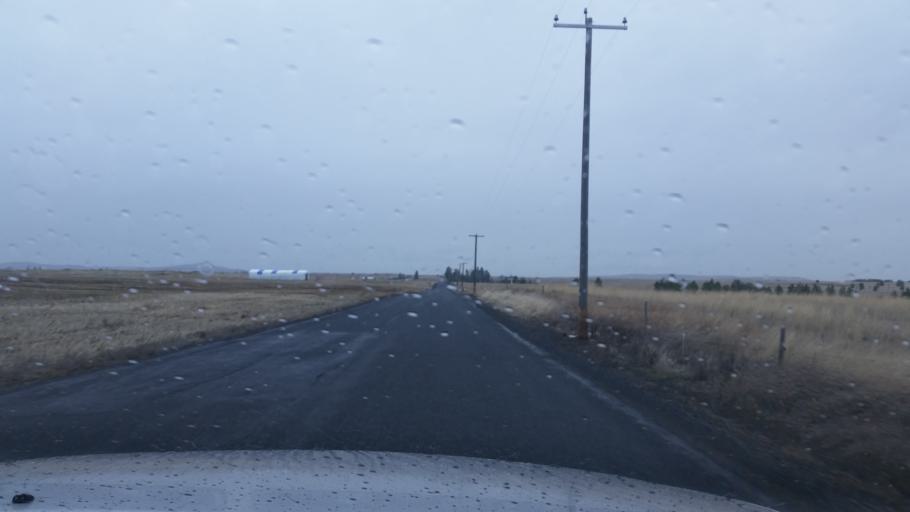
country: US
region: Washington
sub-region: Spokane County
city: Medical Lake
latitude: 47.6144
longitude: -117.7657
